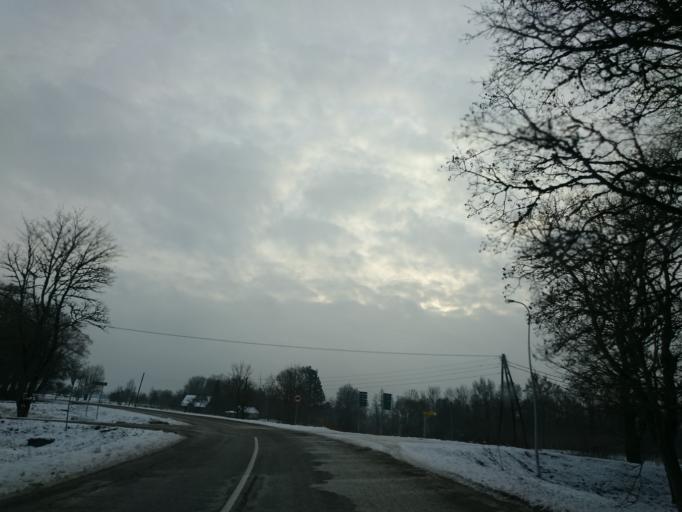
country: LV
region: Seja
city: Loja
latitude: 57.2002
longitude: 24.5937
